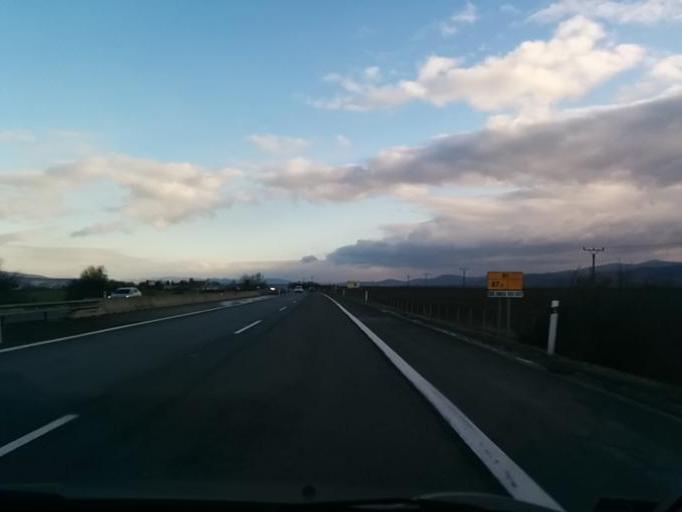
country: SK
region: Trnavsky
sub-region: Okres Trnava
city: Piestany
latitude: 48.6216
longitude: 17.8044
